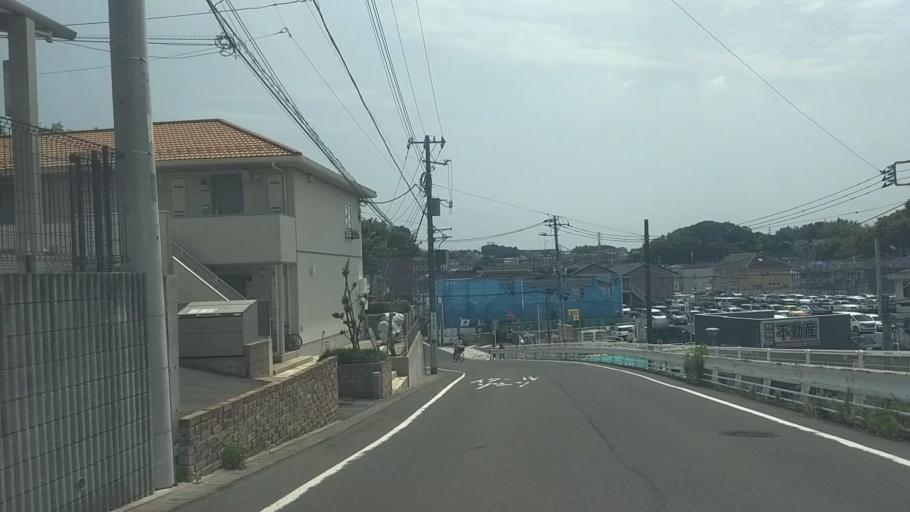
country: JP
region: Kanagawa
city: Yokohama
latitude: 35.5068
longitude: 139.6178
